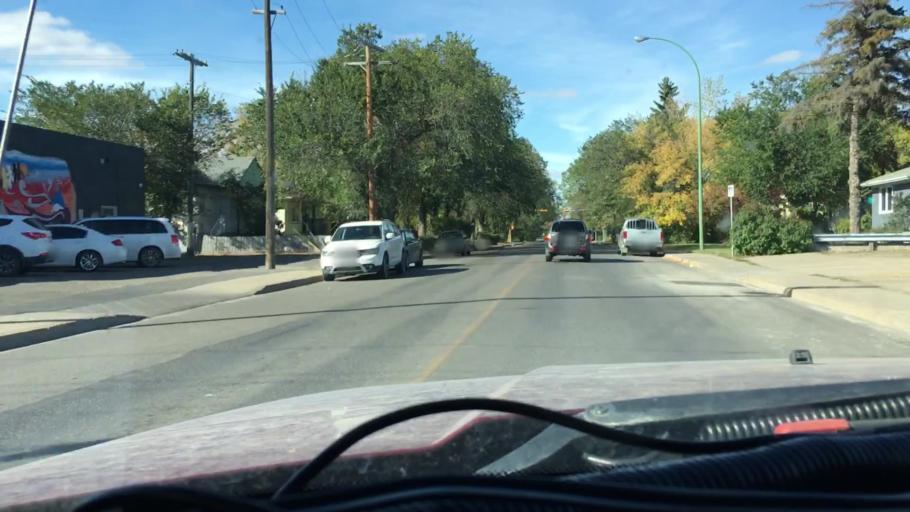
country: CA
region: Saskatchewan
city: Regina
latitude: 50.4615
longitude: -104.6312
